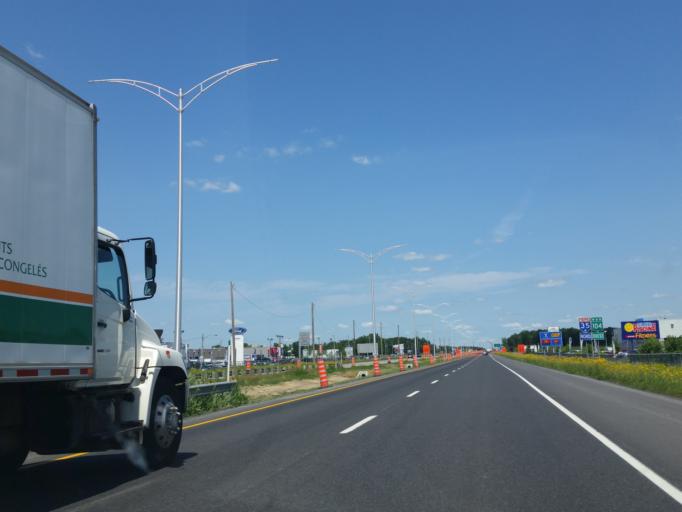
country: CA
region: Quebec
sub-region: Monteregie
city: Saint-Jean-sur-Richelieu
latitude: 45.3352
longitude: -73.2875
